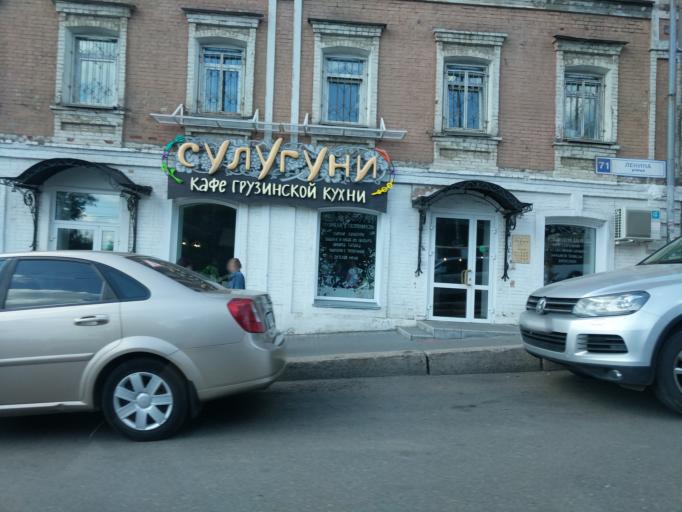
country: RU
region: Kirov
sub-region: Kirovo-Chepetskiy Rayon
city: Kirov
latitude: 58.6034
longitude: 49.6808
